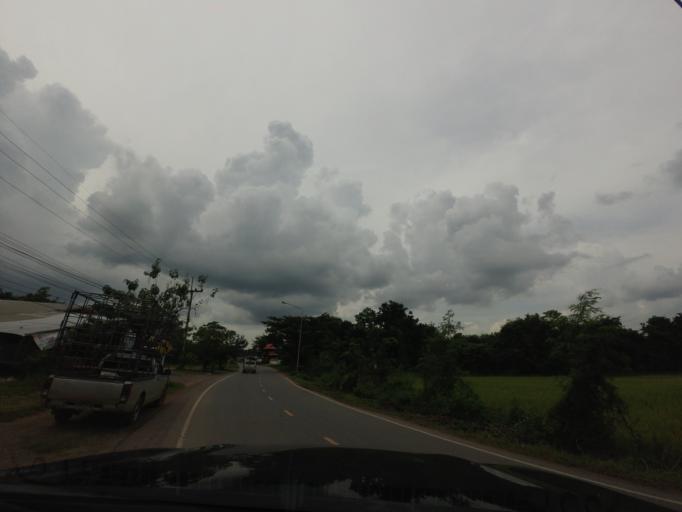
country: TH
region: Changwat Nong Bua Lamphu
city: Nong Bua Lamphu
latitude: 17.2730
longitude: 102.3926
